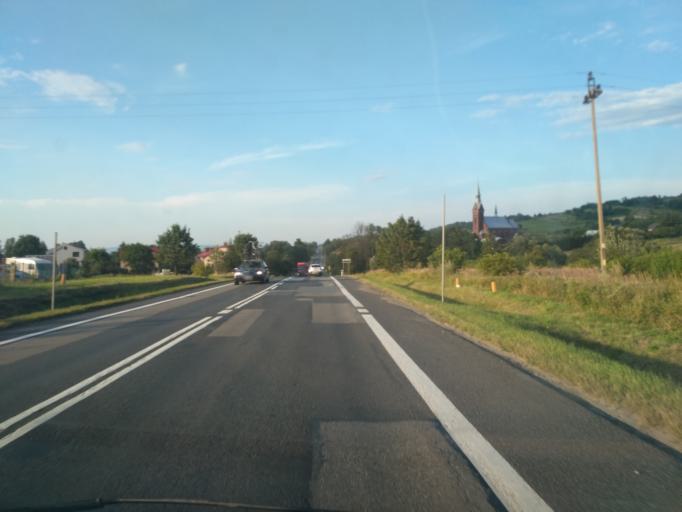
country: PL
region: Subcarpathian Voivodeship
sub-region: Powiat krosnienski
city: Dukla
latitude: 49.5917
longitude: 21.7123
